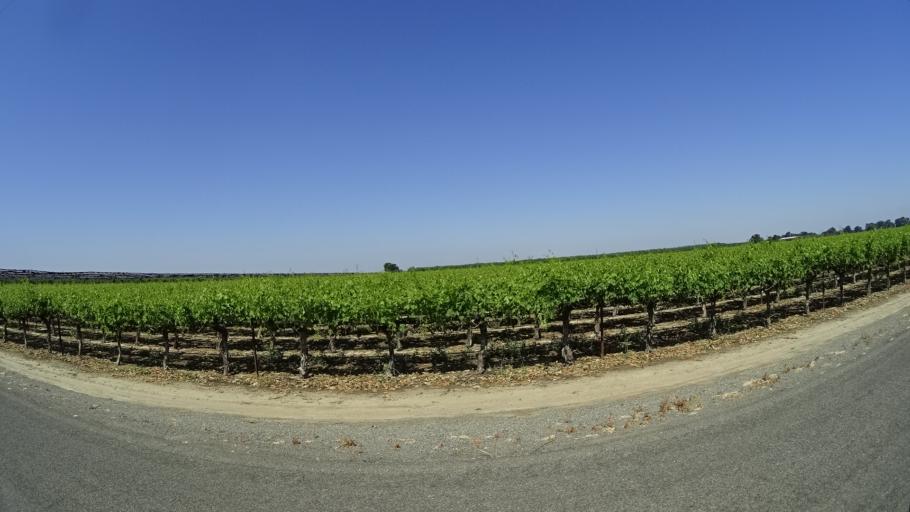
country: US
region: California
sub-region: Kings County
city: Lucerne
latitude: 36.4236
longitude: -119.5828
